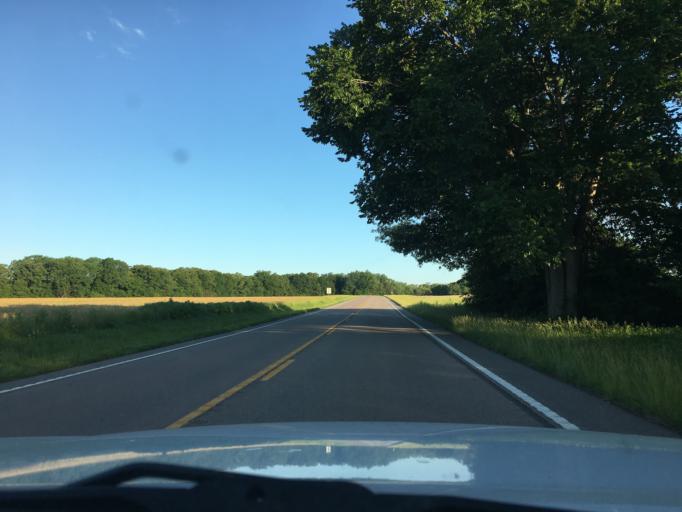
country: US
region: Missouri
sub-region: Gasconade County
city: Owensville
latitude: 38.4548
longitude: -91.4581
